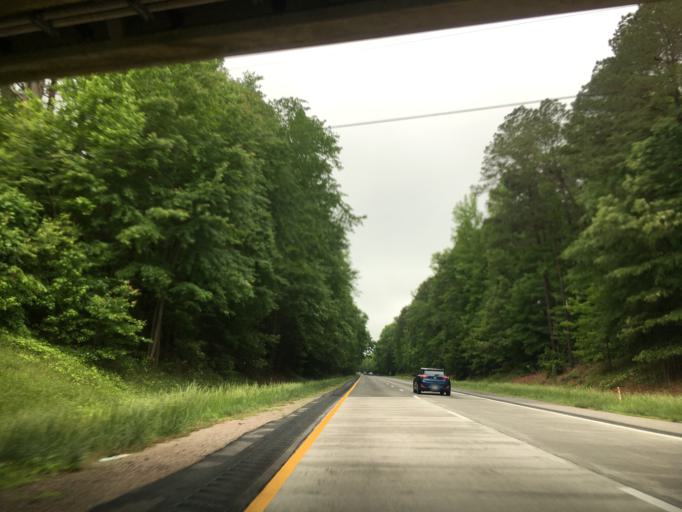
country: US
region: Virginia
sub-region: Dinwiddie County
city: Dinwiddie
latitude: 37.0575
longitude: -77.6005
